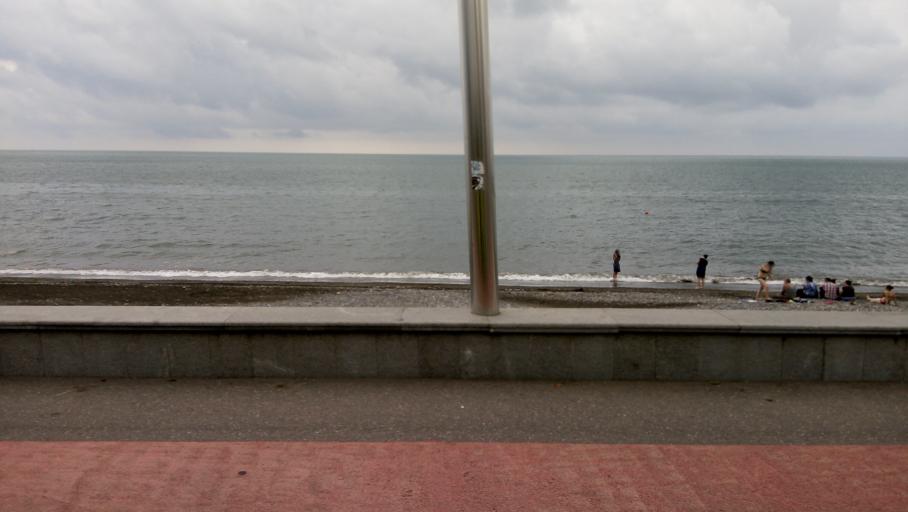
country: GE
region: Ajaria
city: Makhinjauri
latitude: 41.6585
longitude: 41.6764
